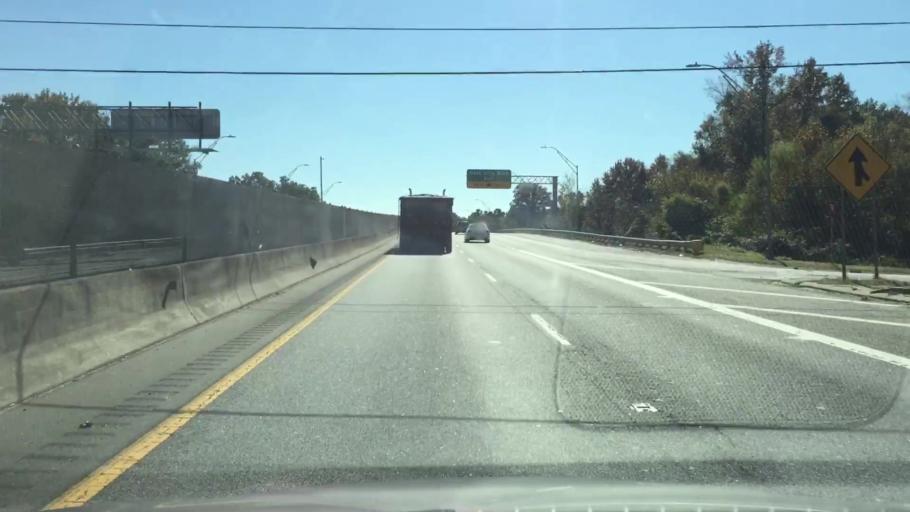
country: US
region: North Carolina
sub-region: Guilford County
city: Greensboro
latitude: 36.0653
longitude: -79.7669
